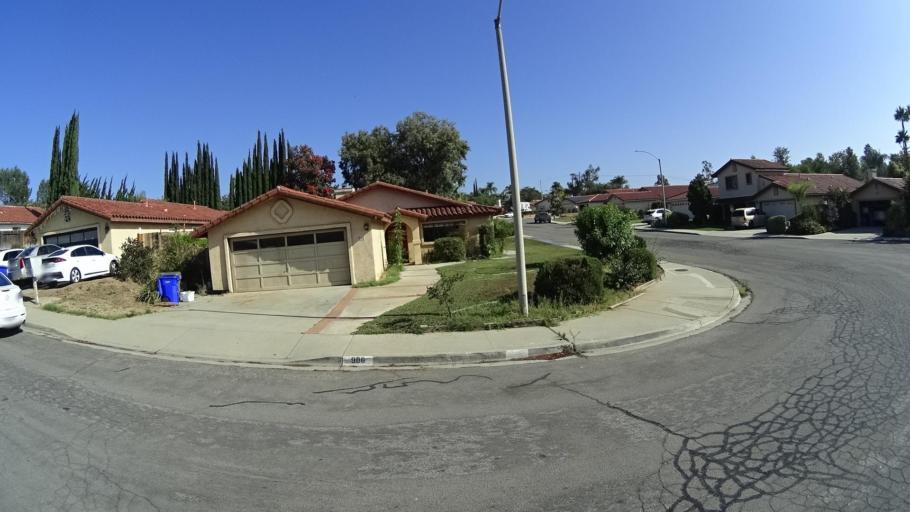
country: US
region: California
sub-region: San Diego County
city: Fallbrook
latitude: 33.3751
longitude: -117.2392
